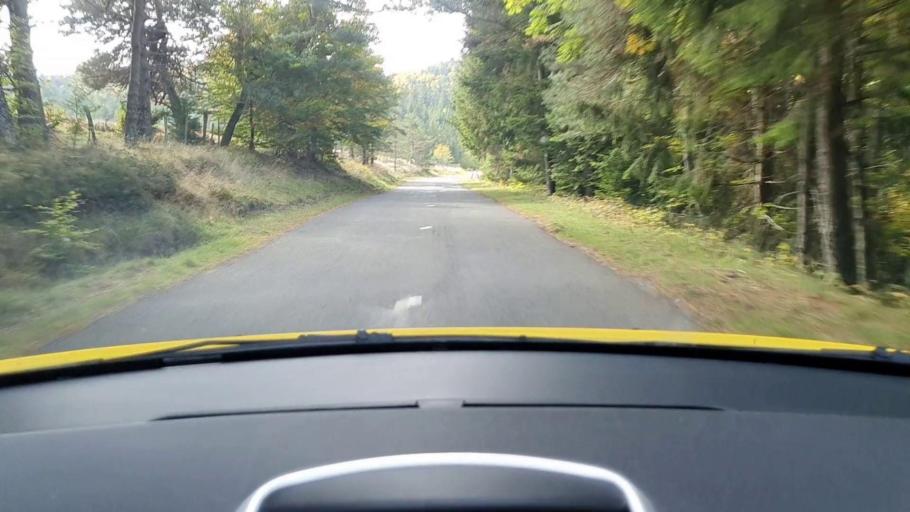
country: FR
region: Languedoc-Roussillon
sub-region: Departement du Gard
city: Valleraugue
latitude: 44.0807
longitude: 3.5628
